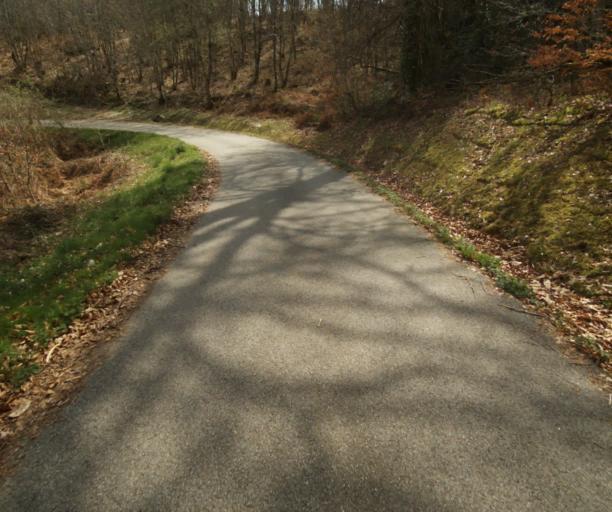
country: FR
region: Limousin
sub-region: Departement de la Correze
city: Naves
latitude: 45.3474
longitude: 1.7999
